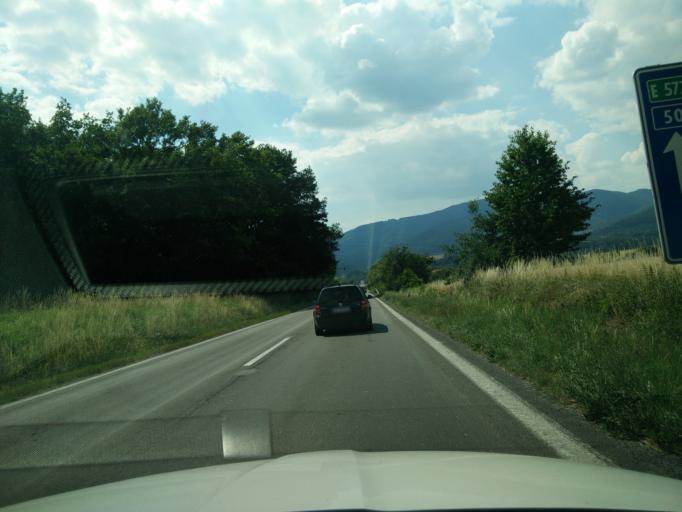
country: SK
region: Nitriansky
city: Novaky
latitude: 48.7207
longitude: 18.5025
